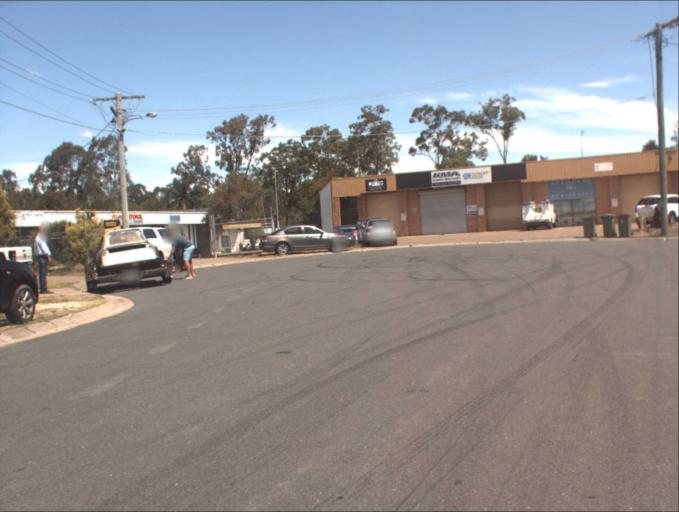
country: AU
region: Queensland
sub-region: Logan
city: Woodridge
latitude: -27.6203
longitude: 153.1068
